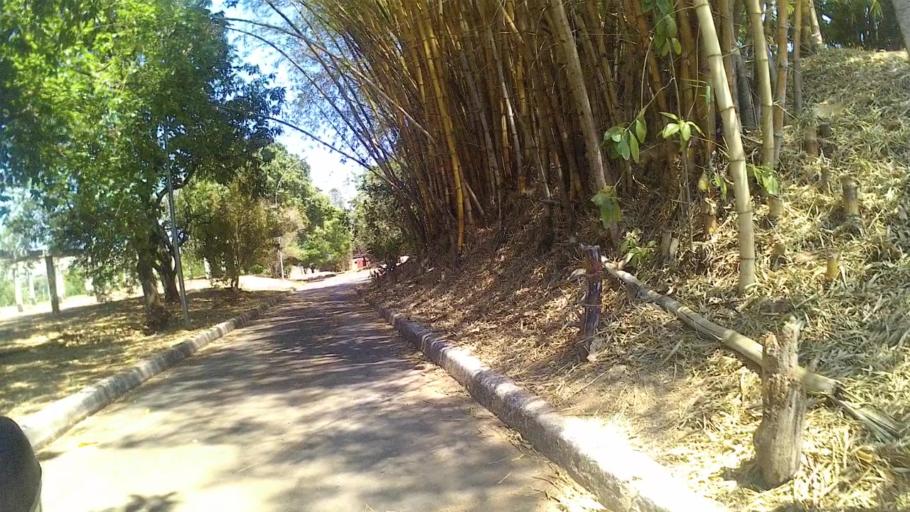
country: BR
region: Federal District
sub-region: Brasilia
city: Brasilia
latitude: -15.7287
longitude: -47.8935
